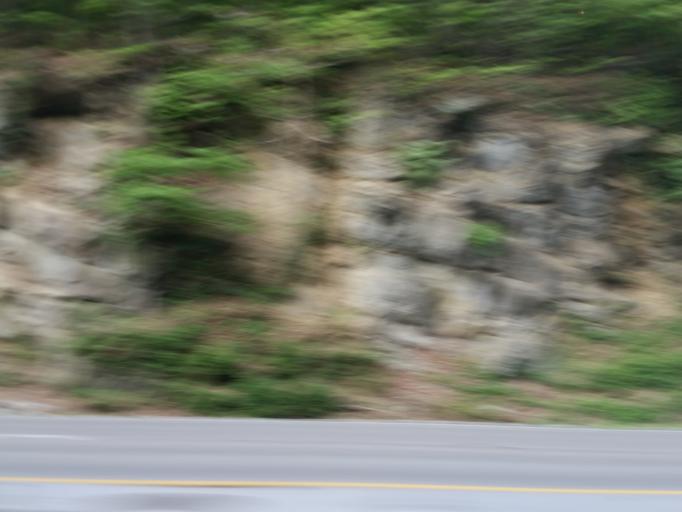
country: US
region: Virginia
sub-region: Washington County
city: Abingdon
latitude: 36.7555
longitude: -82.0575
